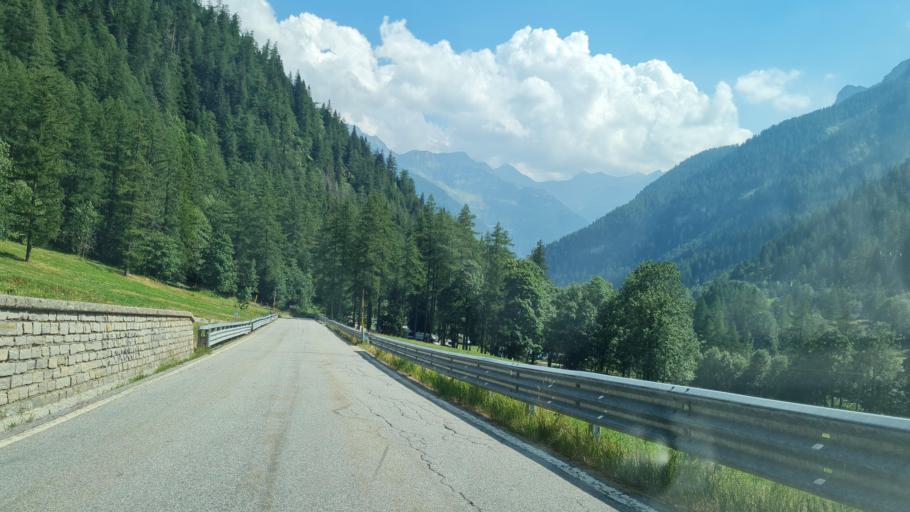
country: IT
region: Piedmont
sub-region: Provincia Verbano-Cusio-Ossola
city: Formazza
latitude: 46.3856
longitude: 8.4246
